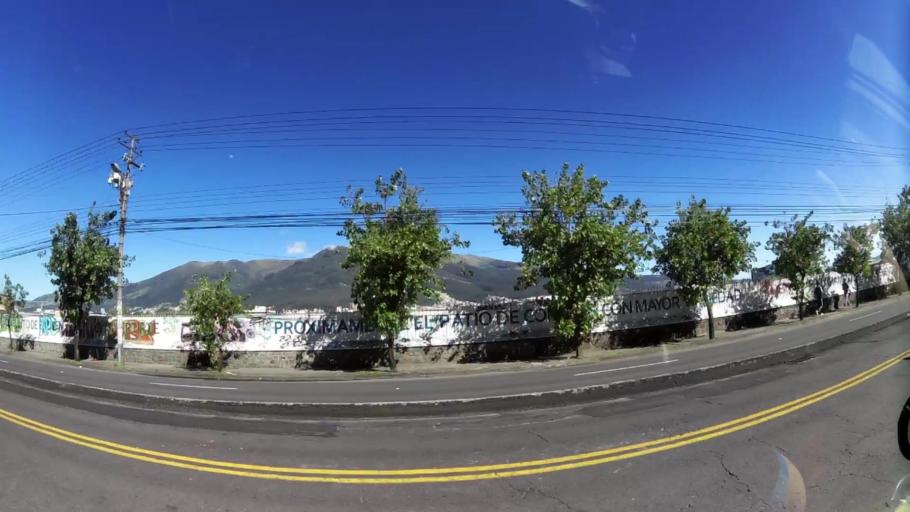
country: EC
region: Pichincha
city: Quito
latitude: -0.1666
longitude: -78.4757
